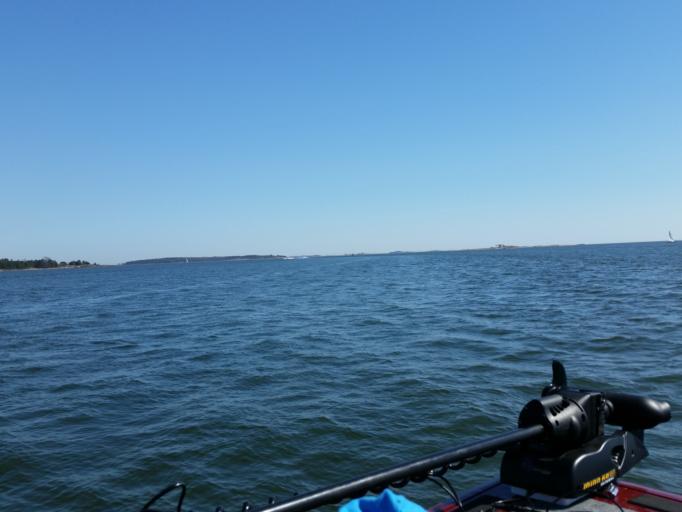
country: FI
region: Uusimaa
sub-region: Helsinki
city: Koukkuniemi
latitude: 60.1411
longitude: 24.8074
